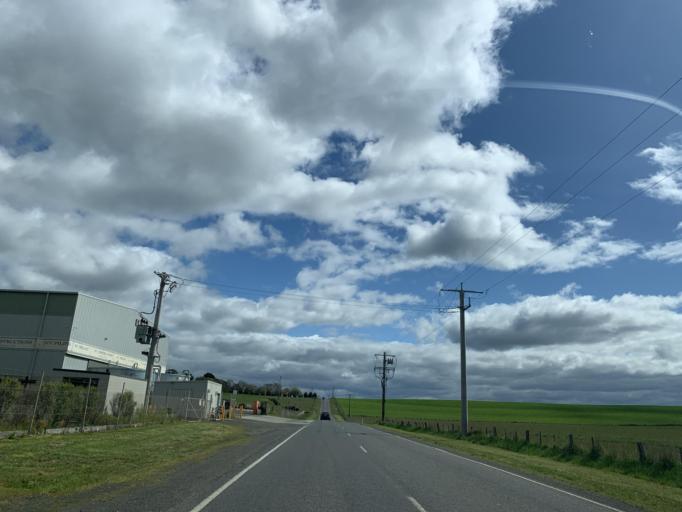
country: AU
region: Victoria
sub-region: Whittlesea
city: Whittlesea
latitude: -37.2808
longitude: 144.9449
